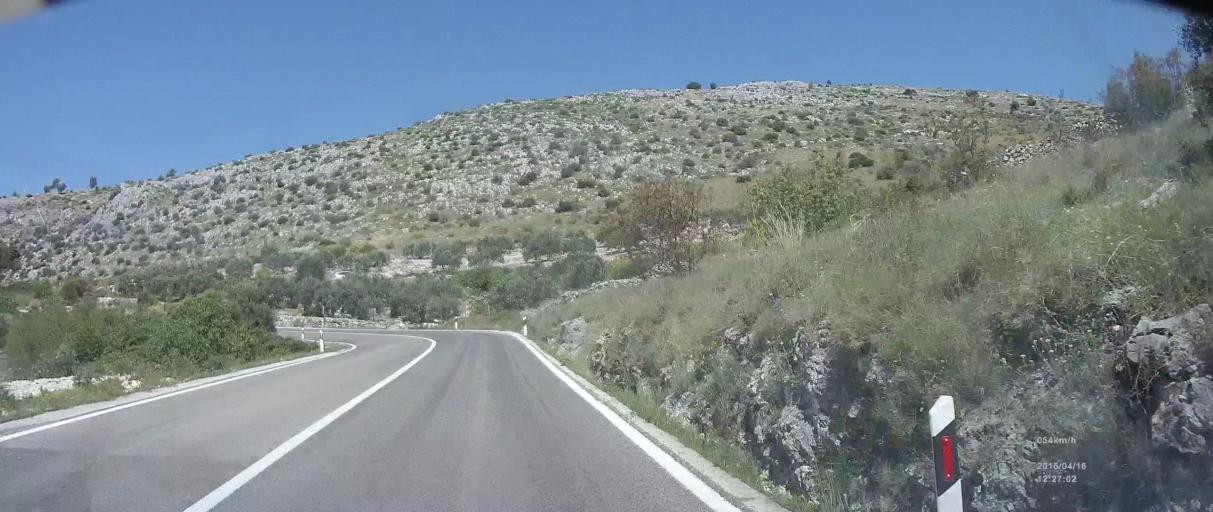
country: HR
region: Splitsko-Dalmatinska
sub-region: Grad Trogir
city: Trogir
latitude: 43.5195
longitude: 16.2038
